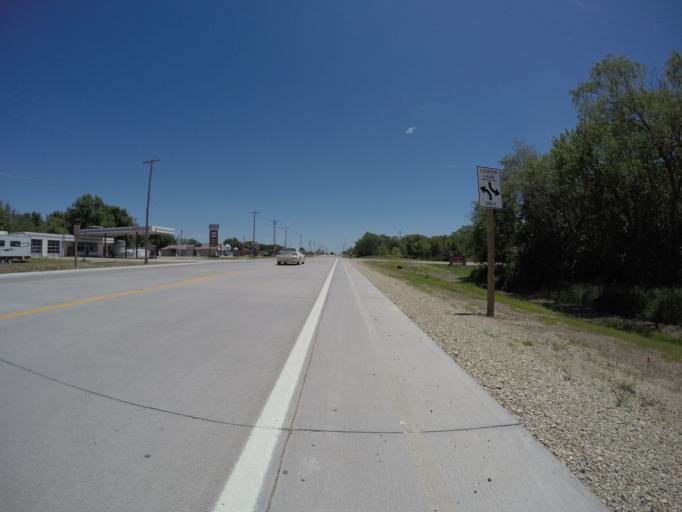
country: US
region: Kansas
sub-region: Republic County
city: Belleville
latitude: 39.8124
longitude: -97.6331
